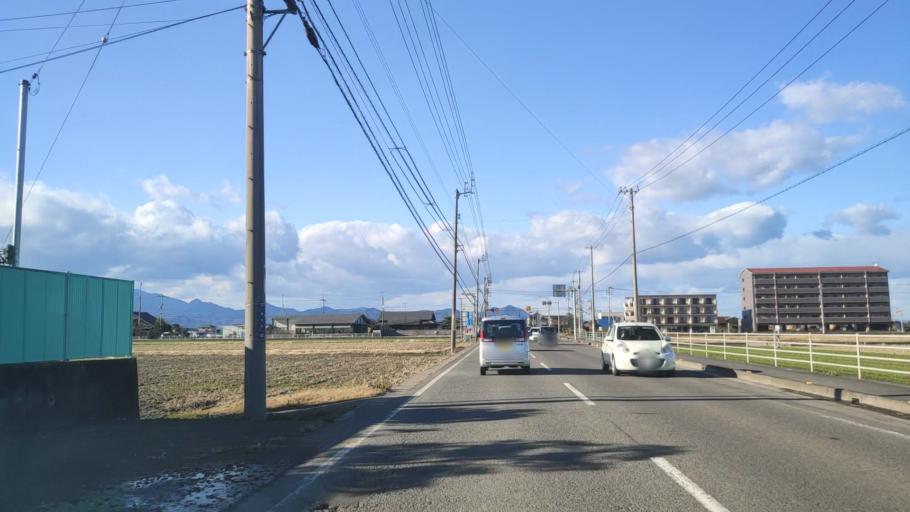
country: JP
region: Ehime
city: Saijo
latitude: 33.9128
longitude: 133.1085
